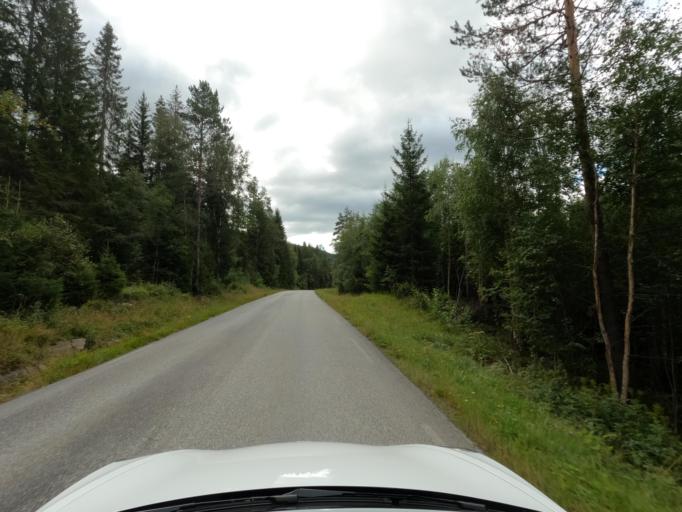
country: NO
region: Buskerud
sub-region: Nore og Uvdal
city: Rodberg
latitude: 60.0245
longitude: 8.8327
